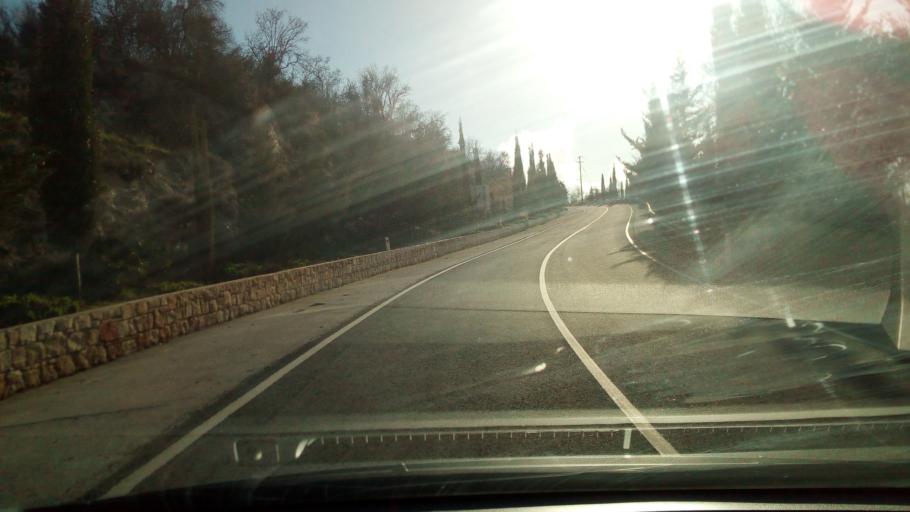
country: CY
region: Pafos
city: Tala
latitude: 34.9217
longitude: 32.5277
